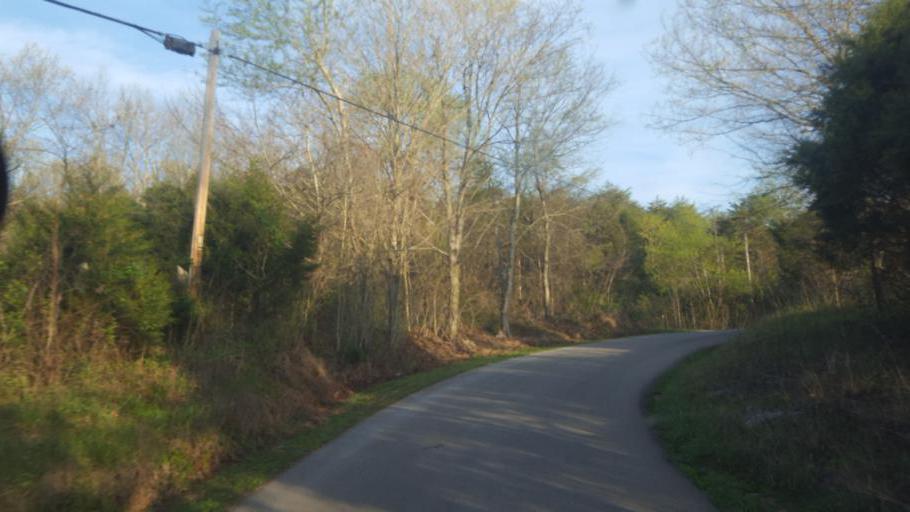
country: US
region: Kentucky
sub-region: Barren County
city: Cave City
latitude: 37.1878
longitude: -86.0124
